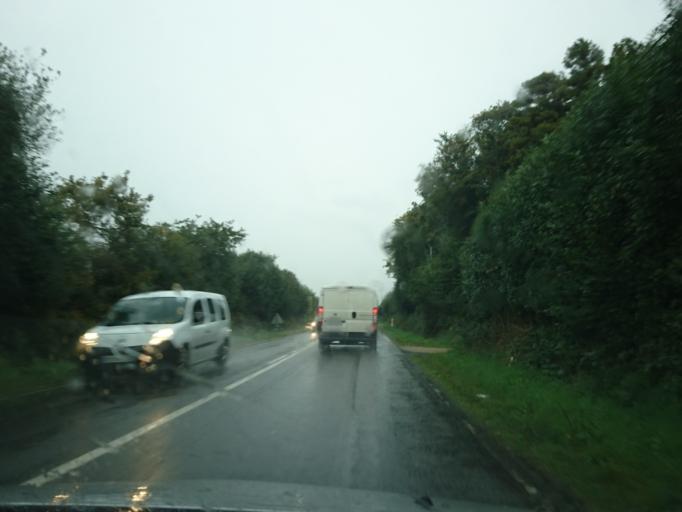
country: FR
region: Brittany
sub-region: Departement du Finistere
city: Gouesnou
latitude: 48.4650
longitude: -4.4490
